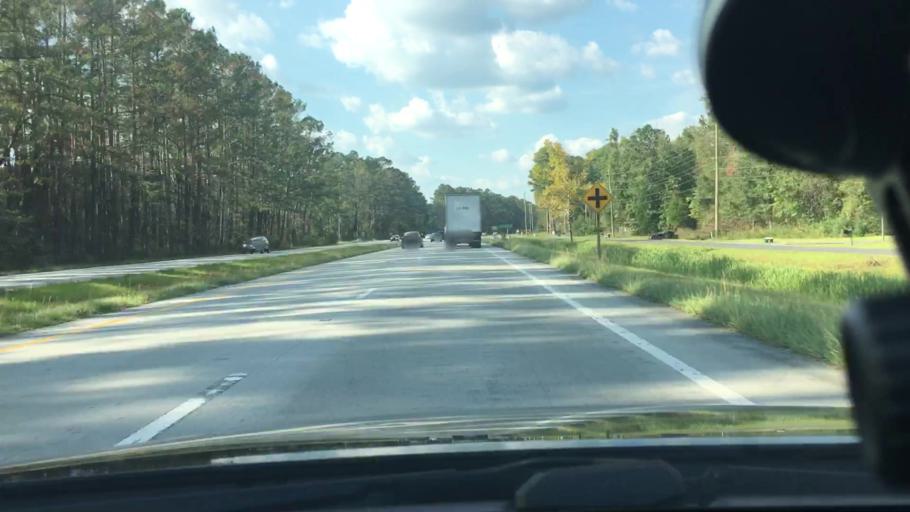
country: US
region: North Carolina
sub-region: Craven County
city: Neuse Forest
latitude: 34.9868
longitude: -76.9808
